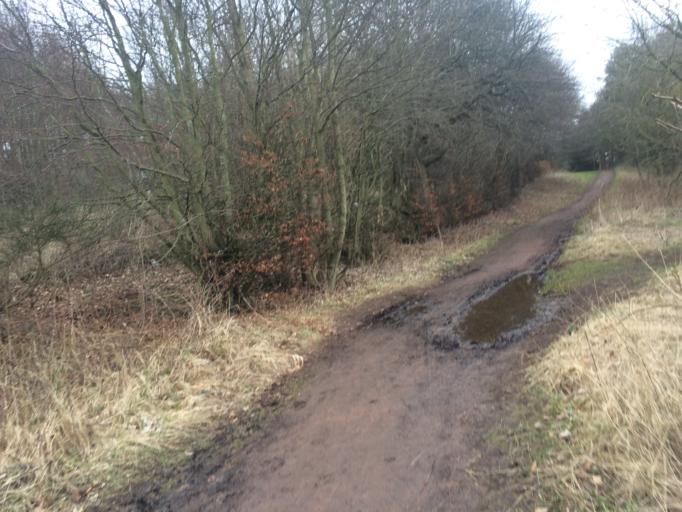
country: GB
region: Scotland
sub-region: Dundee City
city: Dundee
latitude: 56.4858
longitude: -2.9664
